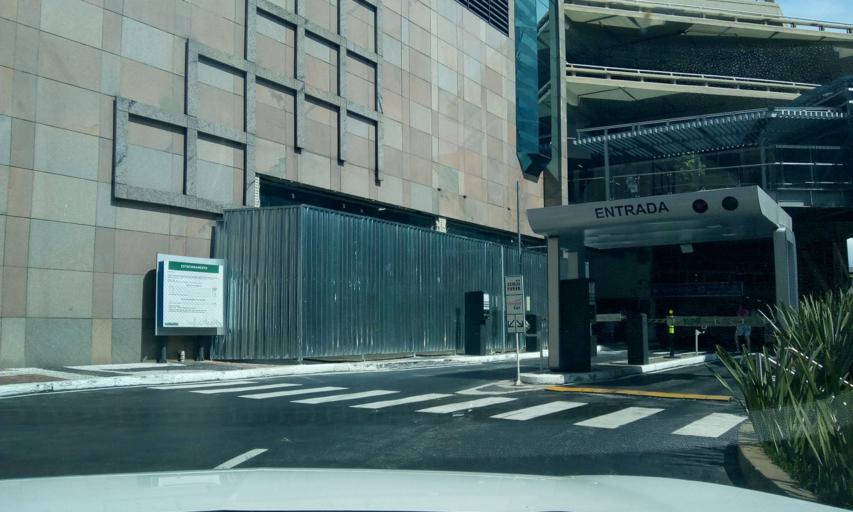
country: BR
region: Sao Paulo
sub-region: Taboao Da Serra
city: Taboao da Serra
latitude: -23.6240
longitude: -46.6999
